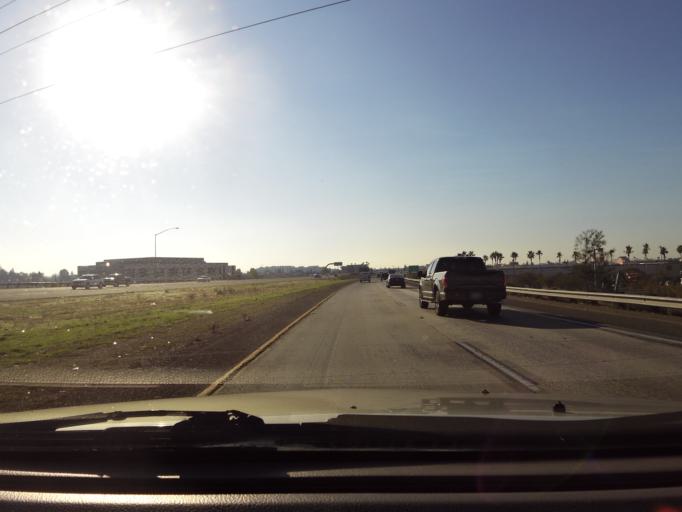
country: US
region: California
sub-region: Fresno County
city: Clovis
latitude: 36.8505
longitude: -119.7864
